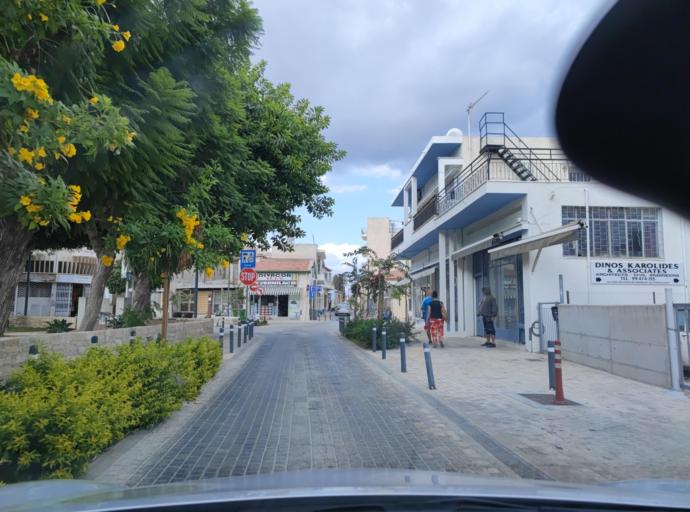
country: CY
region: Limassol
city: Limassol
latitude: 34.6729
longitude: 33.0347
